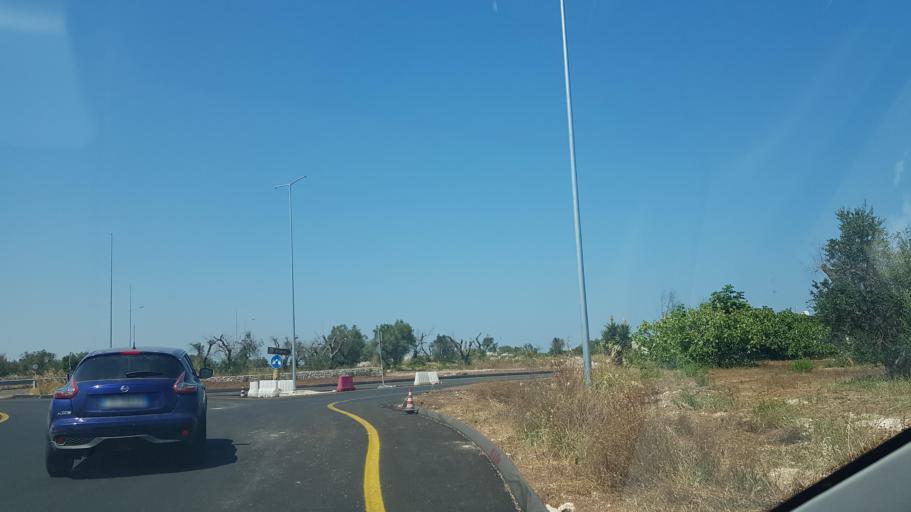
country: IT
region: Apulia
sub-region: Provincia di Lecce
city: Merine
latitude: 40.3348
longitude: 18.2372
